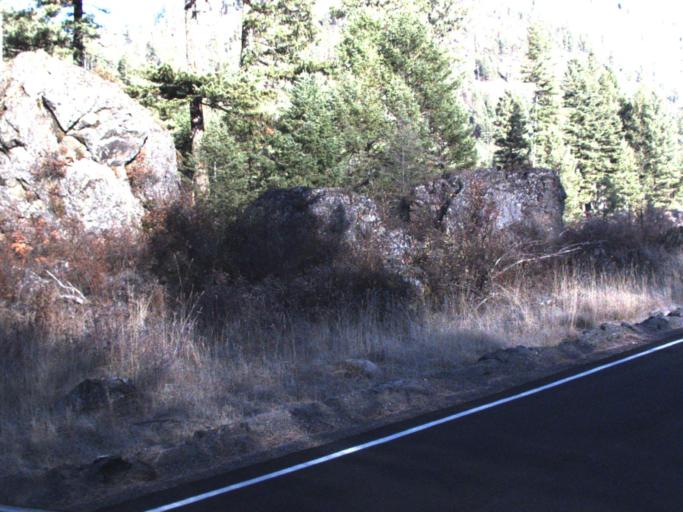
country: US
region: Washington
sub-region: Ferry County
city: Republic
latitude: 48.3760
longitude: -118.7488
